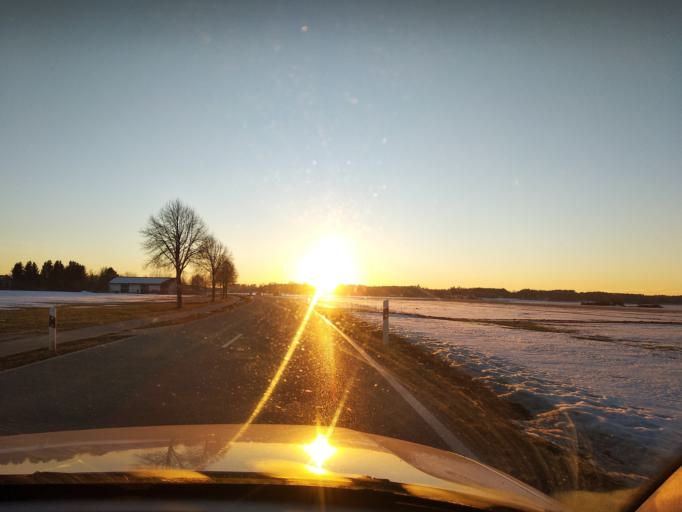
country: DE
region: Bavaria
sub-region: Upper Bavaria
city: Forstern
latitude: 48.1817
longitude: 11.9699
